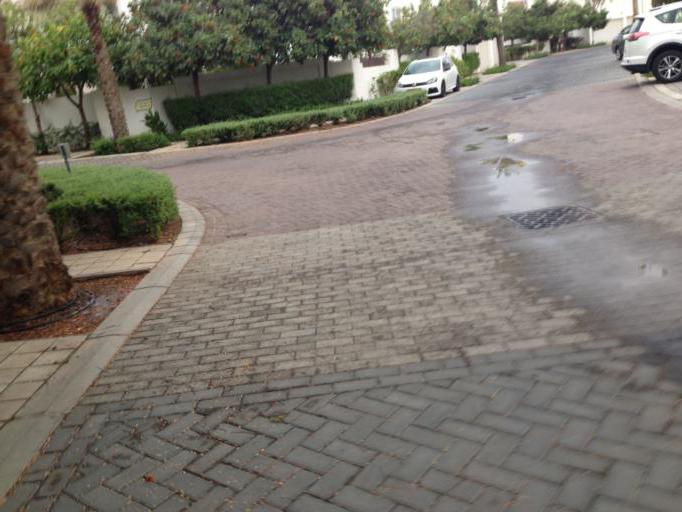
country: OM
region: Muhafazat Masqat
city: As Sib al Jadidah
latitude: 23.6257
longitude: 58.2688
